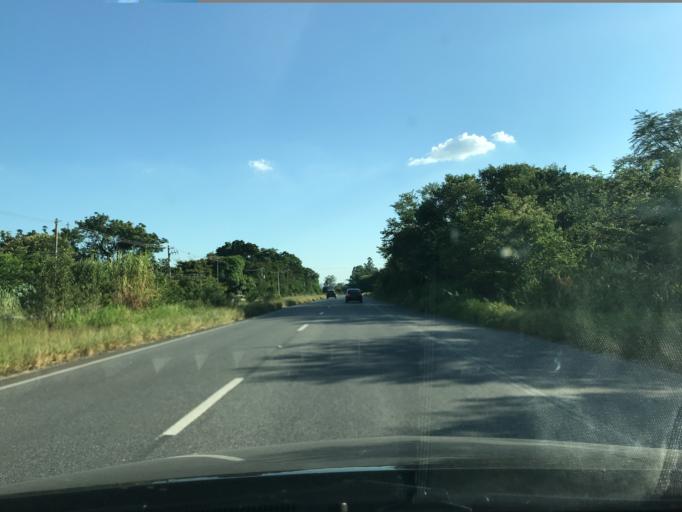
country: BR
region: Sao Paulo
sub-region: Taubate
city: Taubate
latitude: -23.0065
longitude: -45.6399
